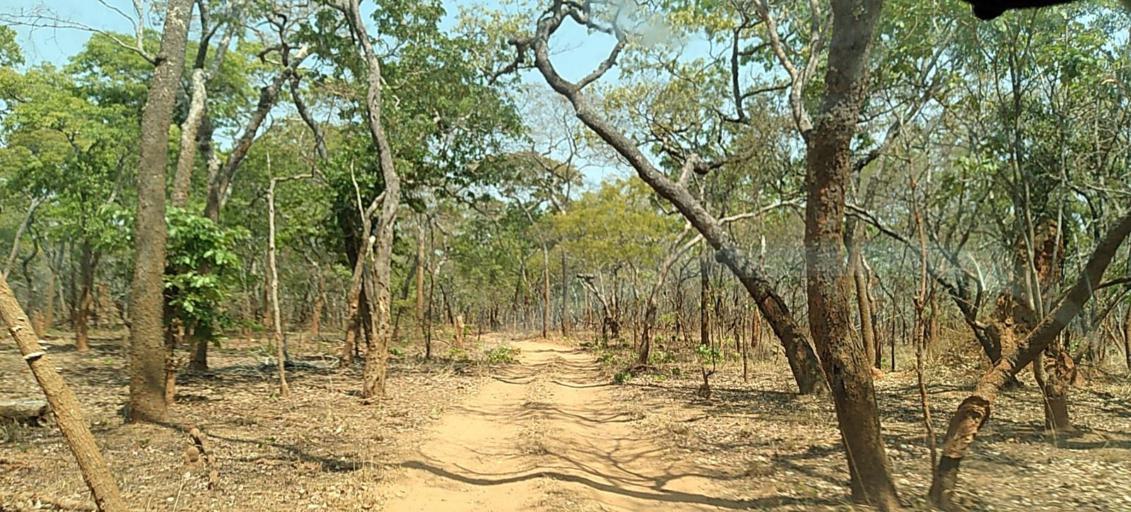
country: ZM
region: North-Western
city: Kasempa
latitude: -13.3941
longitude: 25.5839
